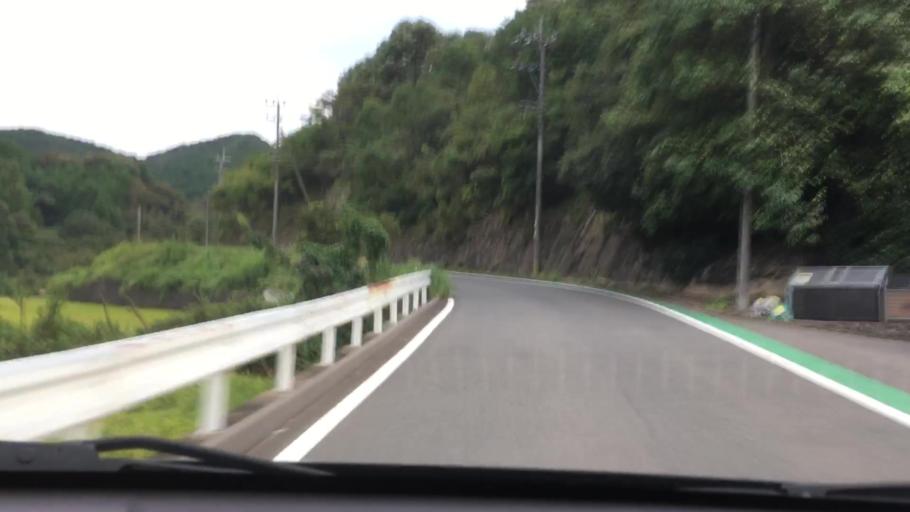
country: JP
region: Nagasaki
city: Sasebo
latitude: 32.9948
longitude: 129.7321
